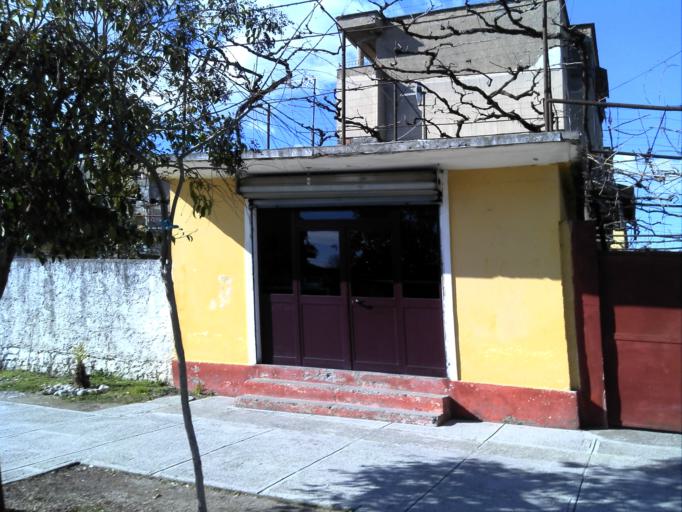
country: AL
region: Shkoder
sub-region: Rrethi i Shkodres
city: Shkoder
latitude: 42.0773
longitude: 19.5262
